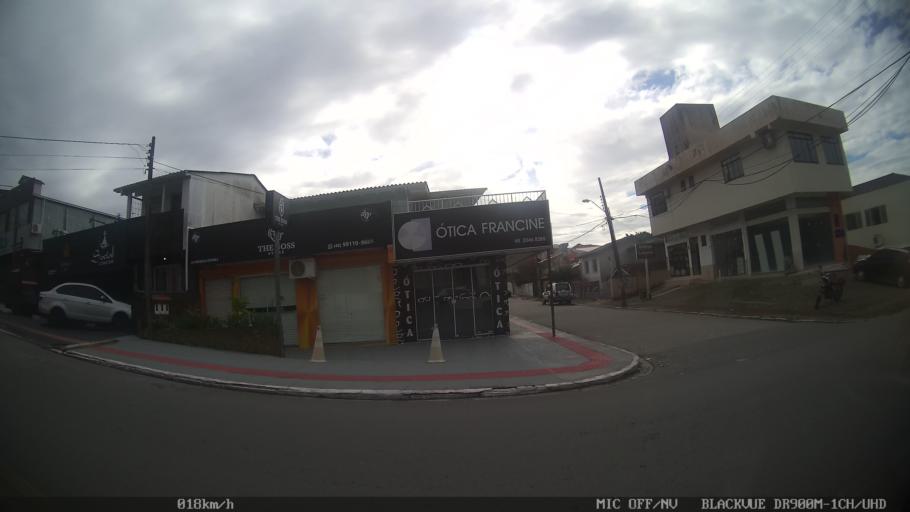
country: BR
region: Santa Catarina
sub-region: Sao Jose
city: Campinas
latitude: -27.5705
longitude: -48.6179
